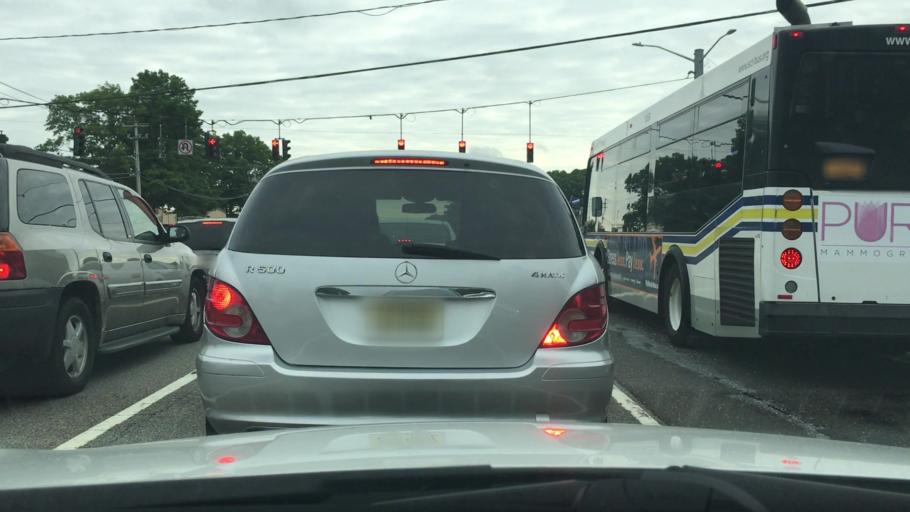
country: US
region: New York
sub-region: Suffolk County
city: Lake Grove
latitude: 40.8729
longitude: -73.1241
